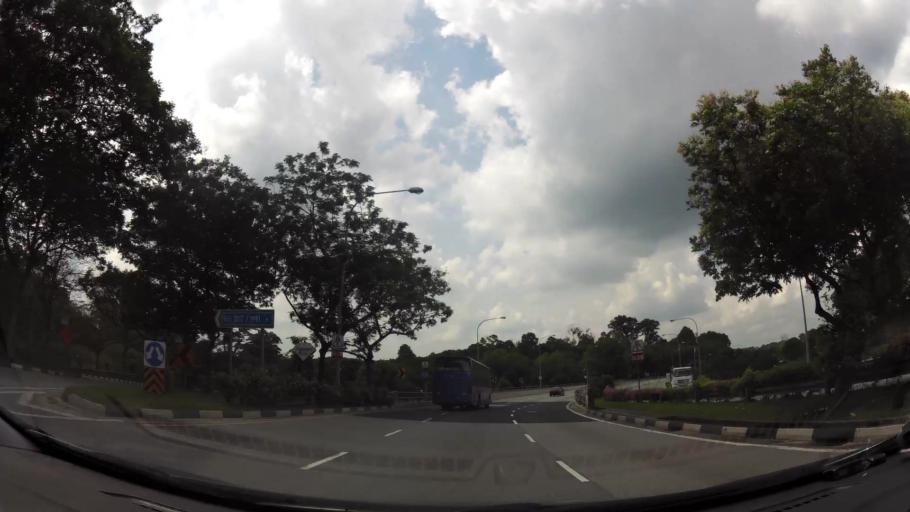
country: MY
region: Johor
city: Johor Bahru
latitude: 1.4143
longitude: 103.8066
